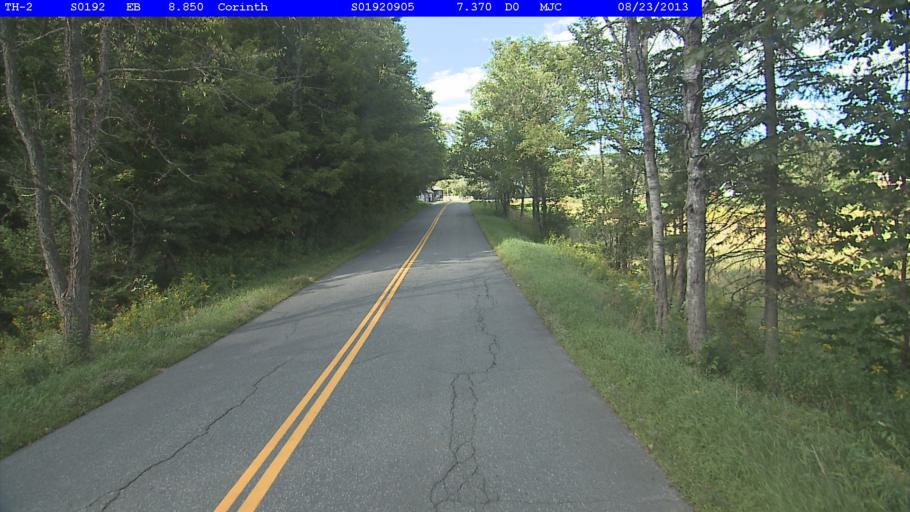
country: US
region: New Hampshire
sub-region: Grafton County
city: Orford
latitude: 44.0142
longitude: -72.2339
